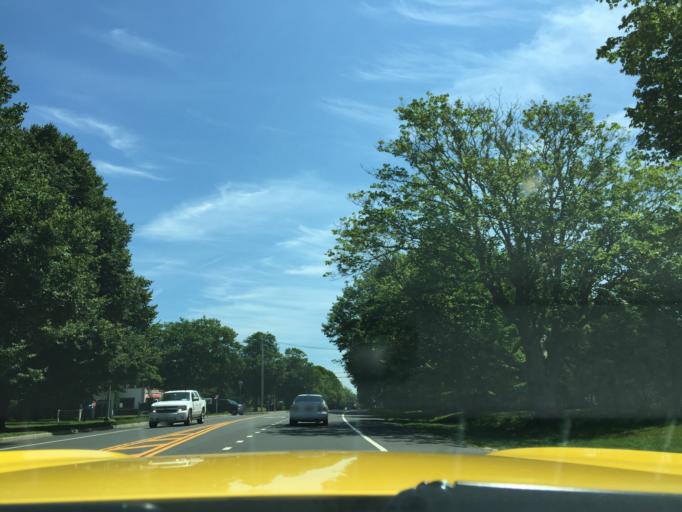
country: US
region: New York
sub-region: Suffolk County
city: East Hampton
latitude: 40.9677
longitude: -72.1710
